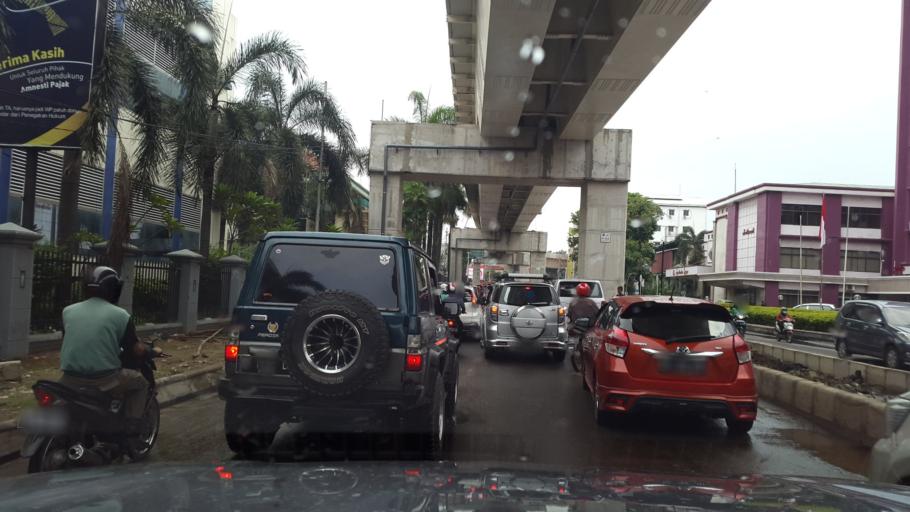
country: ID
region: South Sumatra
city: Plaju
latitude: -2.9774
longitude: 104.7518
